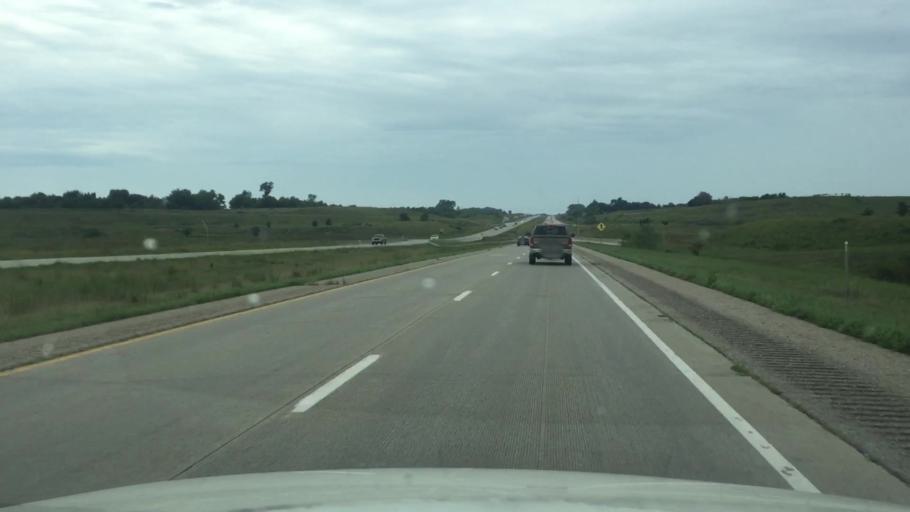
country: US
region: Iowa
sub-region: Warren County
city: Norwalk
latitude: 41.5142
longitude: -93.6788
